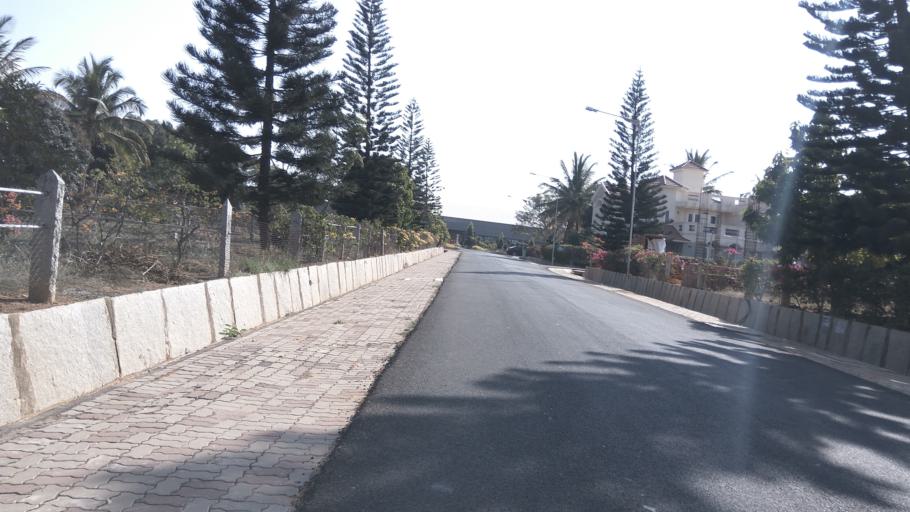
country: IN
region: Karnataka
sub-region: Bangalore Rural
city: Devanhalli
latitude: 13.2070
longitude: 77.6306
